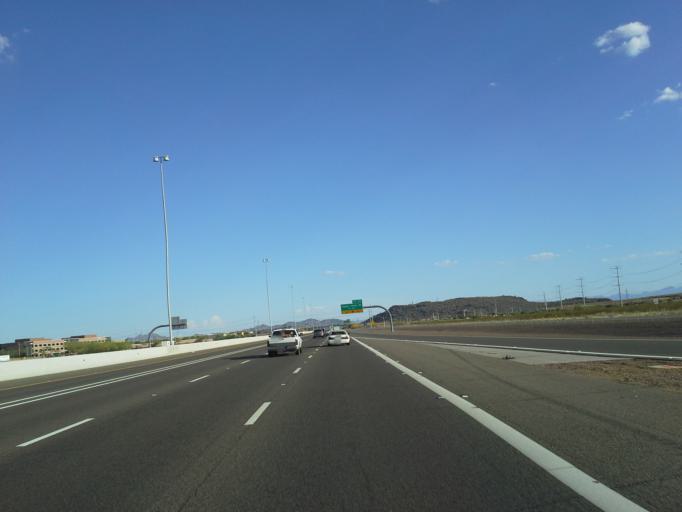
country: US
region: Arizona
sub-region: Maricopa County
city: Anthem
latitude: 33.7228
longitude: -112.1197
